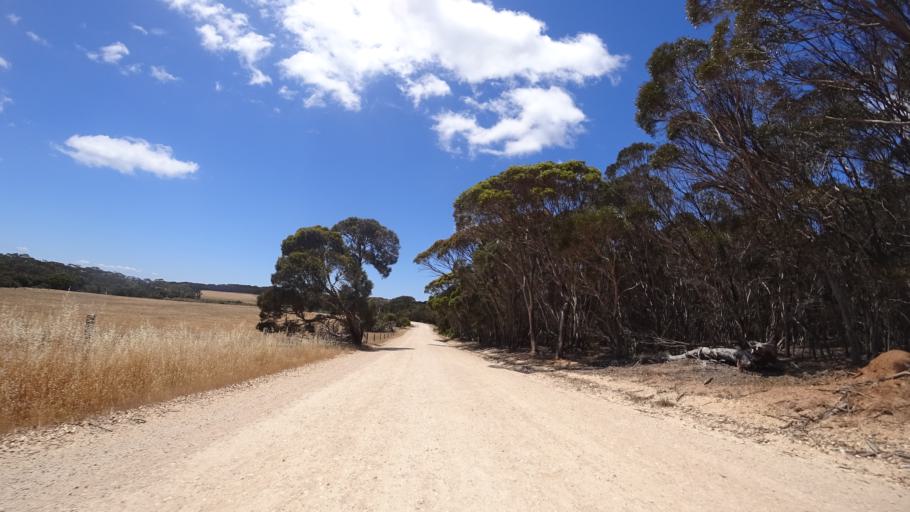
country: AU
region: South Australia
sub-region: Kangaroo Island
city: Kingscote
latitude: -35.8222
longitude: 138.0462
